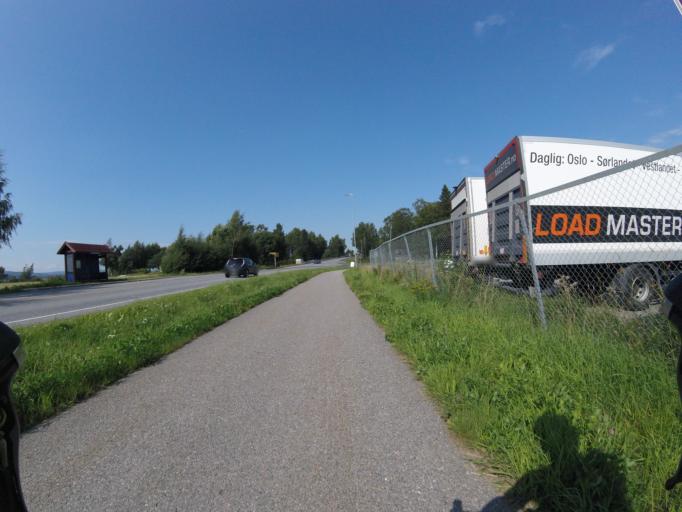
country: NO
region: Akershus
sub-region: Sorum
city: Frogner
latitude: 60.0377
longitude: 11.1132
